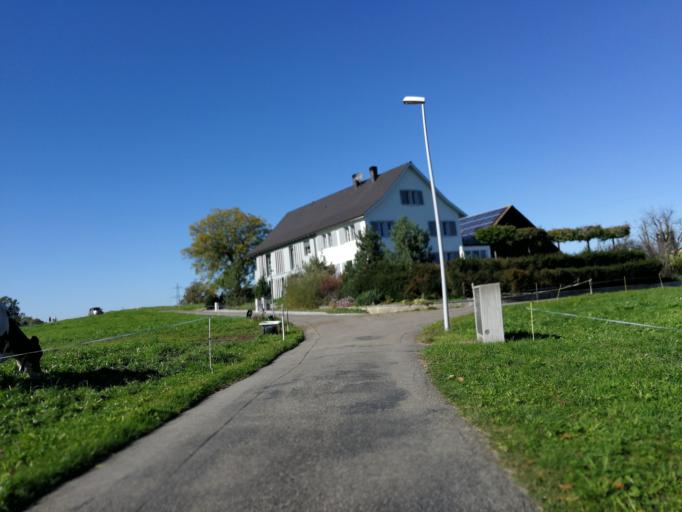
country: CH
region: Zurich
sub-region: Bezirk Hinwil
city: Wolfhausen
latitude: 47.2641
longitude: 8.7908
